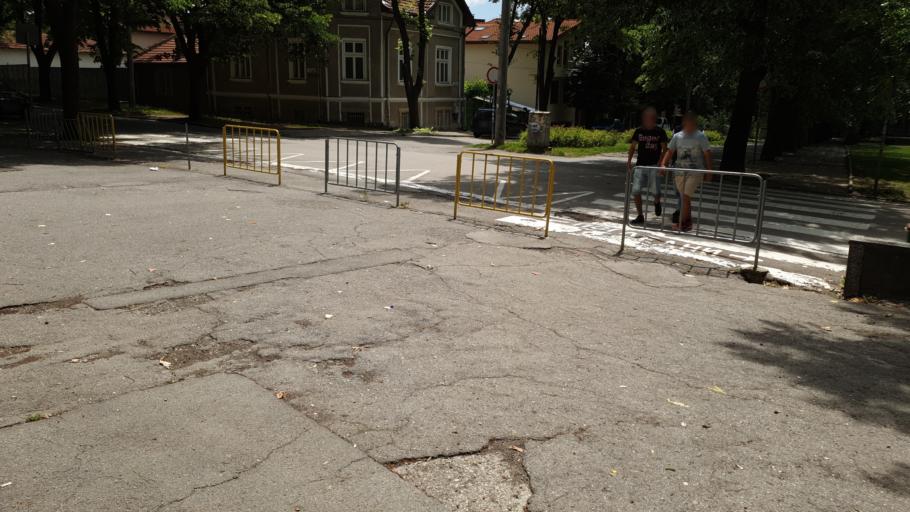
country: BG
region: Razgrad
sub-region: Obshtina Razgrad
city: Razgrad
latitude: 43.5305
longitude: 26.5306
